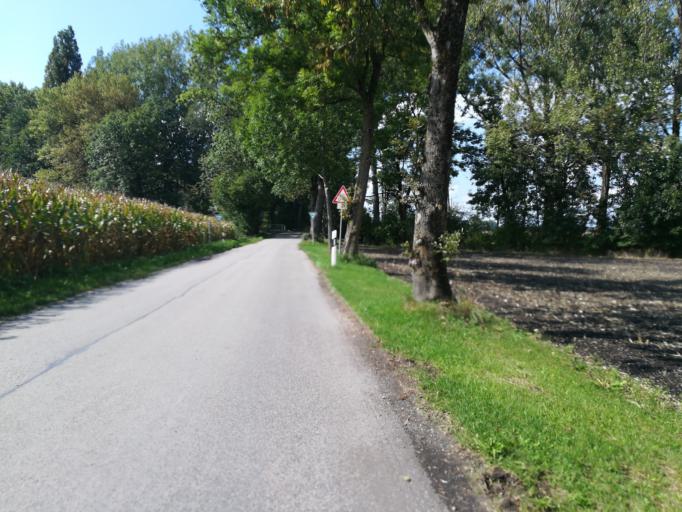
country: DE
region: Bavaria
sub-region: Upper Bavaria
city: Karlsfeld
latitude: 48.2269
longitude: 11.5117
